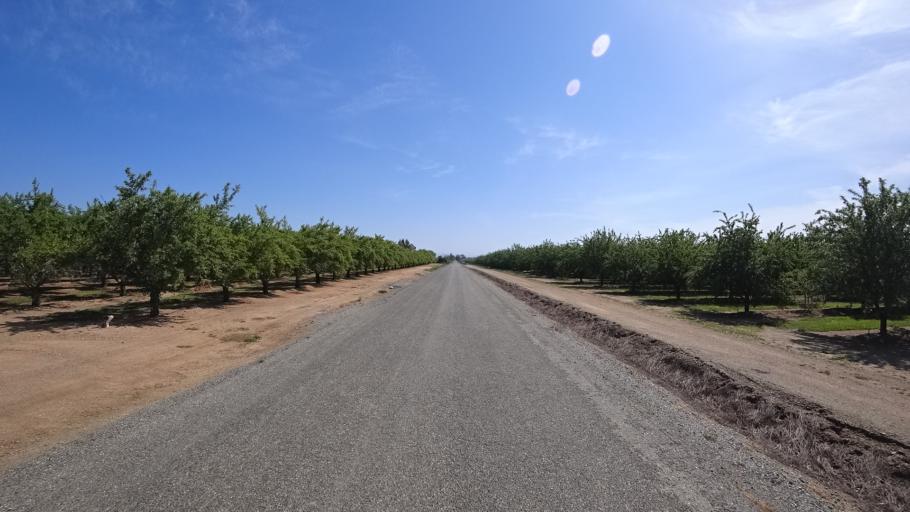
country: US
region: California
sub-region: Glenn County
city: Hamilton City
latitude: 39.8042
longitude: -122.0928
